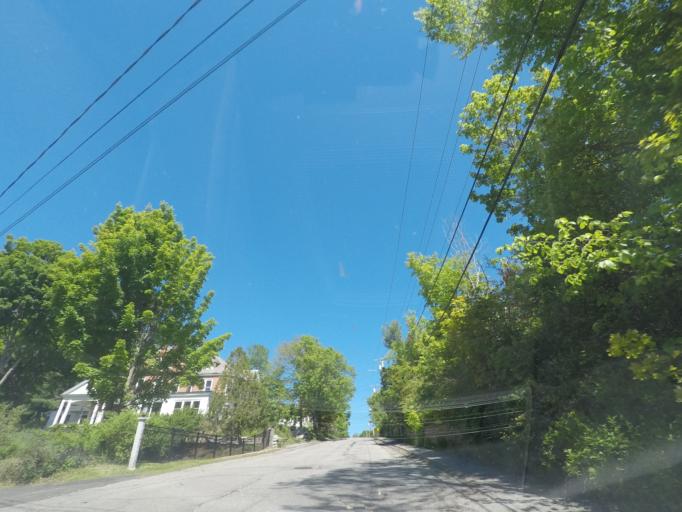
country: US
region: Maine
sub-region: Kennebec County
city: Gardiner
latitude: 44.2310
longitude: -69.7791
